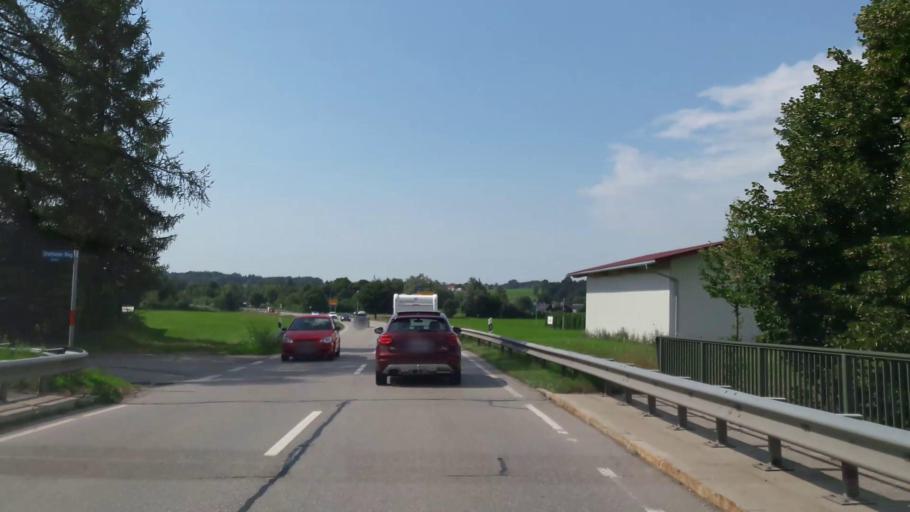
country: DE
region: Bavaria
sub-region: Upper Bavaria
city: Teisendorf
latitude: 47.8459
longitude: 12.8130
